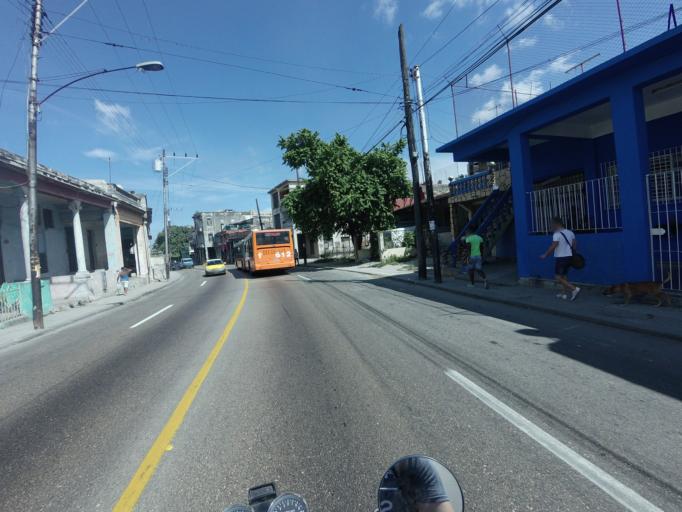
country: CU
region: La Habana
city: Diez de Octubre
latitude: 23.1013
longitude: -82.3630
